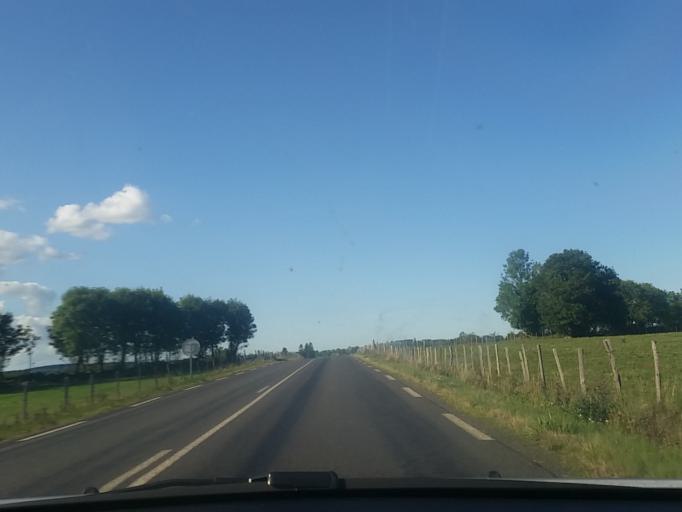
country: FR
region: Auvergne
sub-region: Departement du Cantal
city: Neuveglise
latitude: 44.9644
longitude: 3.0124
